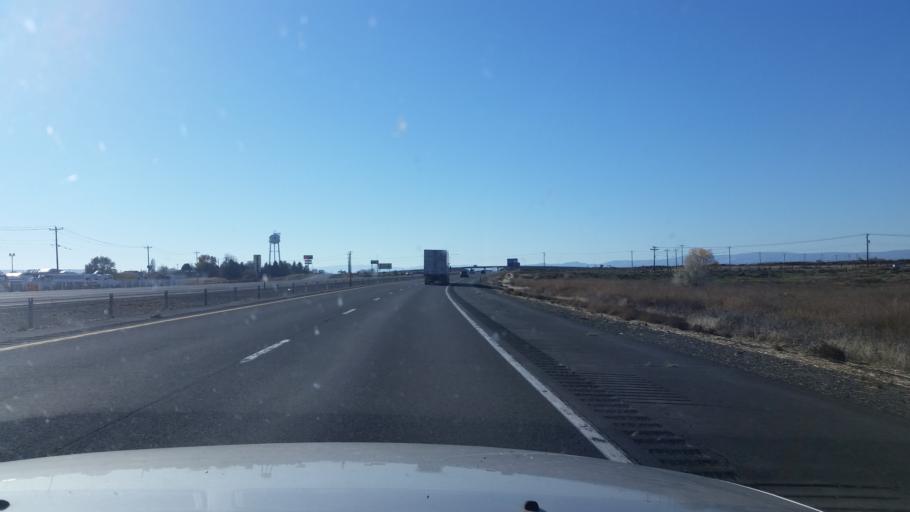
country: US
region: Washington
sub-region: Grant County
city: Quincy
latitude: 47.0904
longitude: -119.8507
